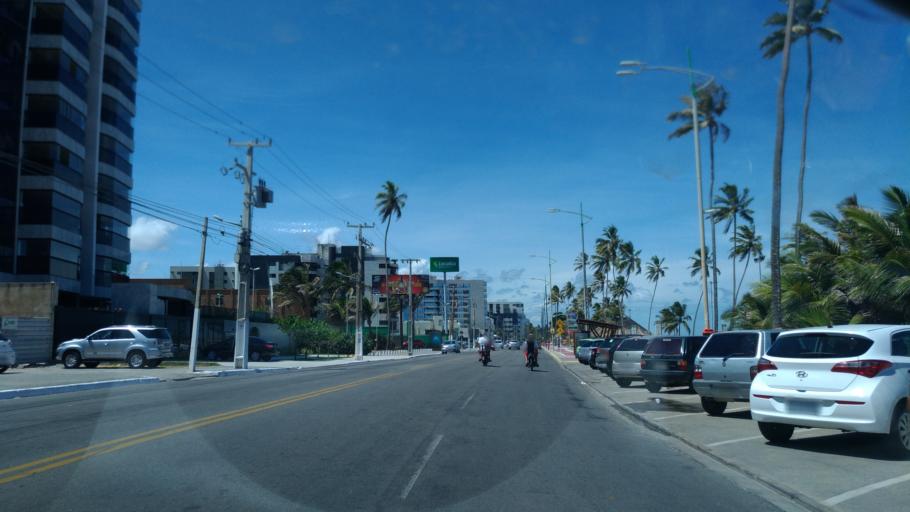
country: BR
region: Alagoas
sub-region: Maceio
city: Maceio
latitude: -9.6482
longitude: -35.7004
